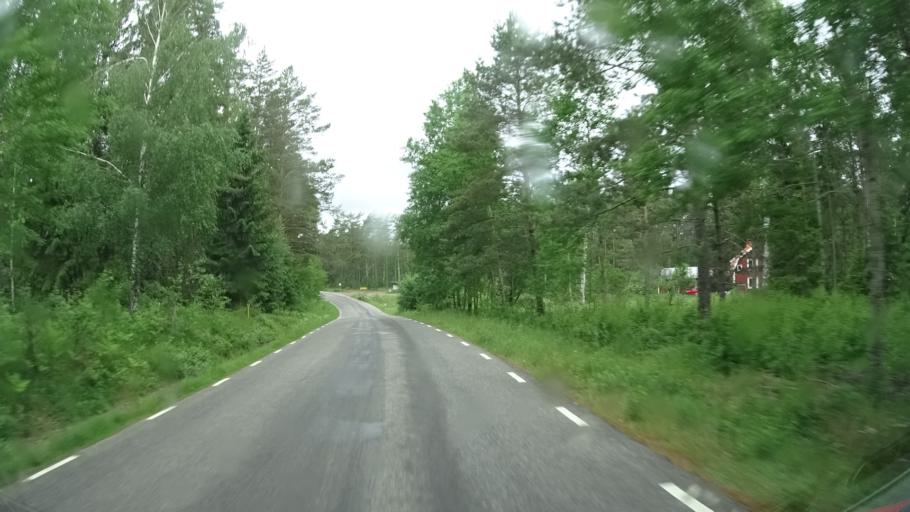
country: SE
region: Joenkoeping
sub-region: Eksjo Kommun
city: Mariannelund
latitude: 57.7032
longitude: 15.6356
